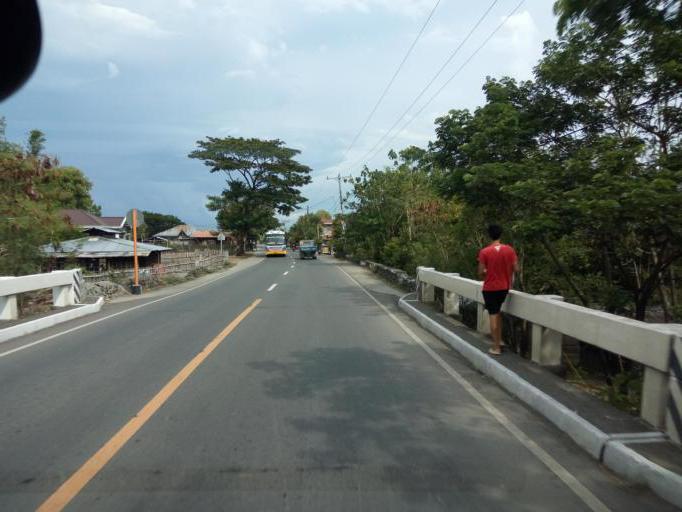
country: PH
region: Central Luzon
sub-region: Province of Nueva Ecija
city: Sibul
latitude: 15.8168
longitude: 120.9587
